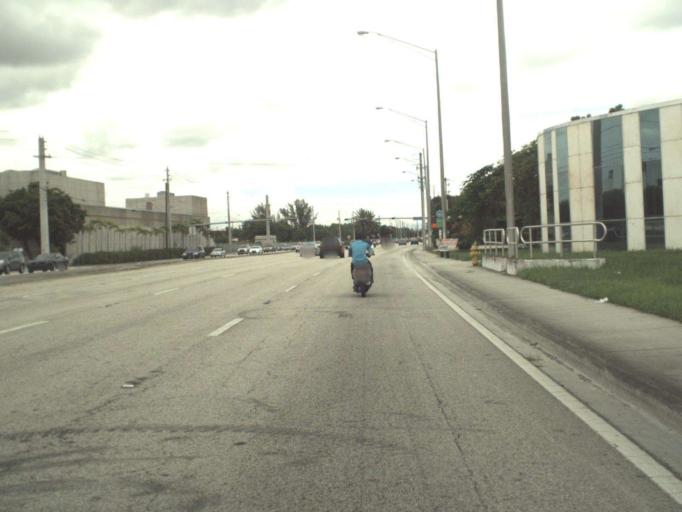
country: US
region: Florida
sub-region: Miami-Dade County
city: North Miami Beach
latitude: 25.9177
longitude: -80.1560
